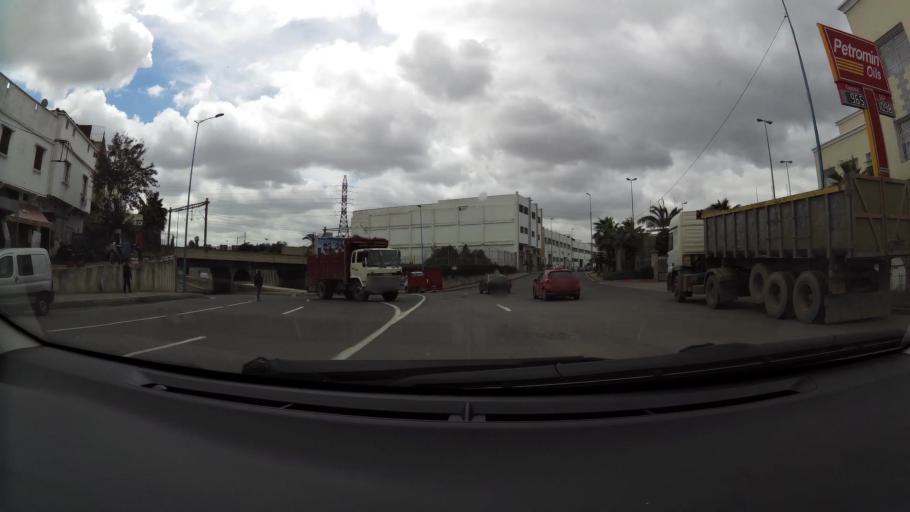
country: MA
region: Grand Casablanca
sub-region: Casablanca
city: Casablanca
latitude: 33.6014
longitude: -7.5455
